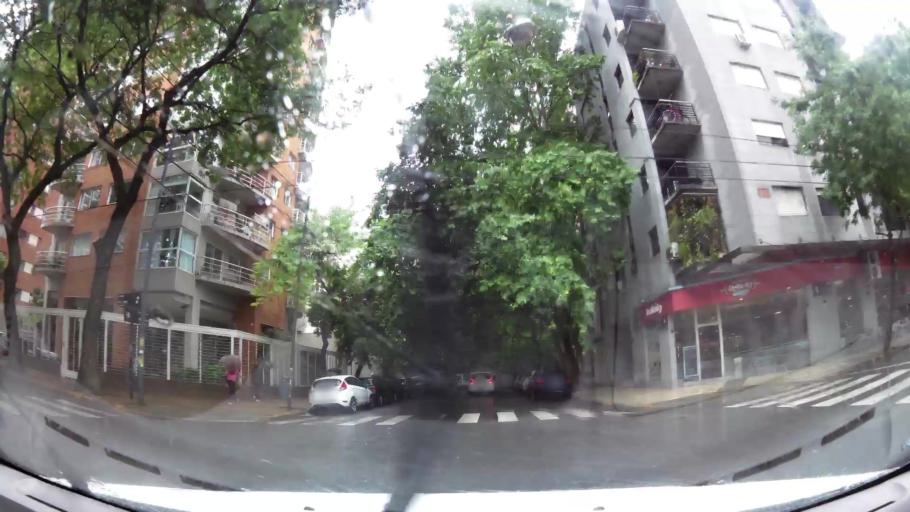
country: AR
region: Buenos Aires F.D.
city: Colegiales
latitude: -34.5769
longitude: -58.4236
